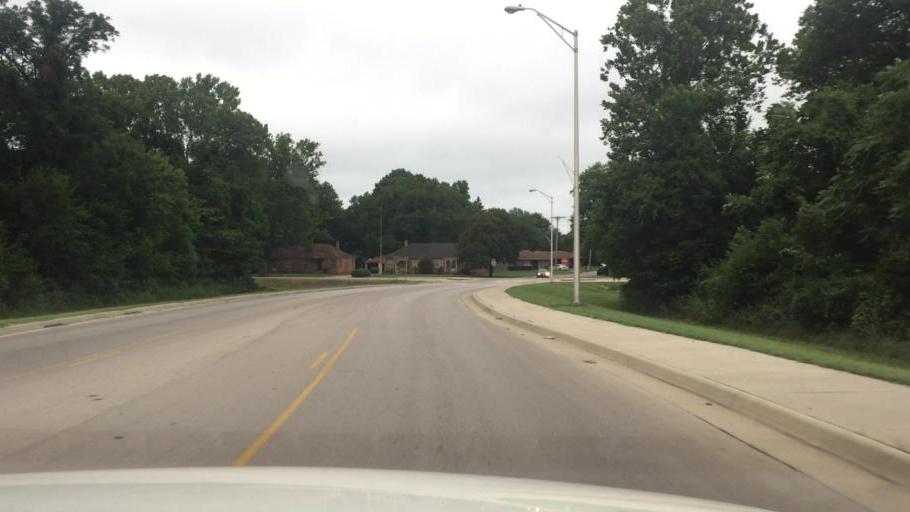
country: US
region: Kansas
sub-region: Montgomery County
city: Coffeyville
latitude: 37.0352
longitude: -95.6469
